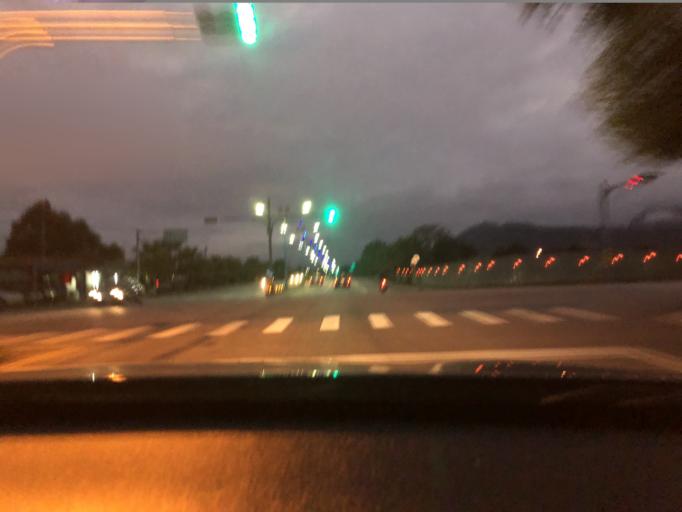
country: TW
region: Taiwan
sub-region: Hualien
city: Hualian
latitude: 23.9563
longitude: 121.5616
